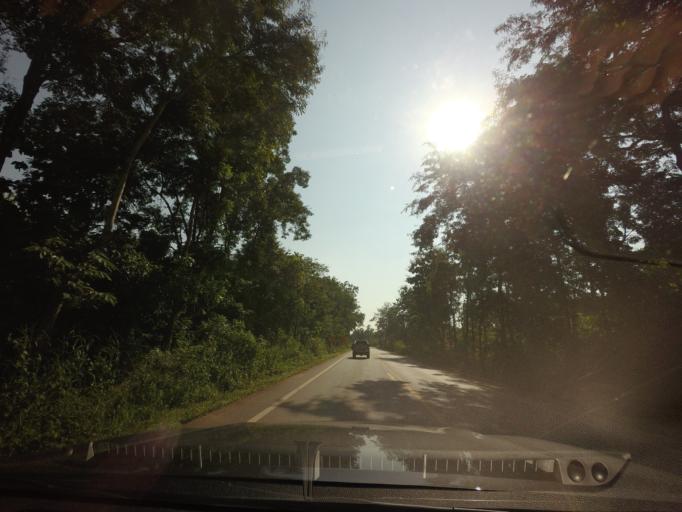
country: TH
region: Nan
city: Nan
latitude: 18.8107
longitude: 100.8022
